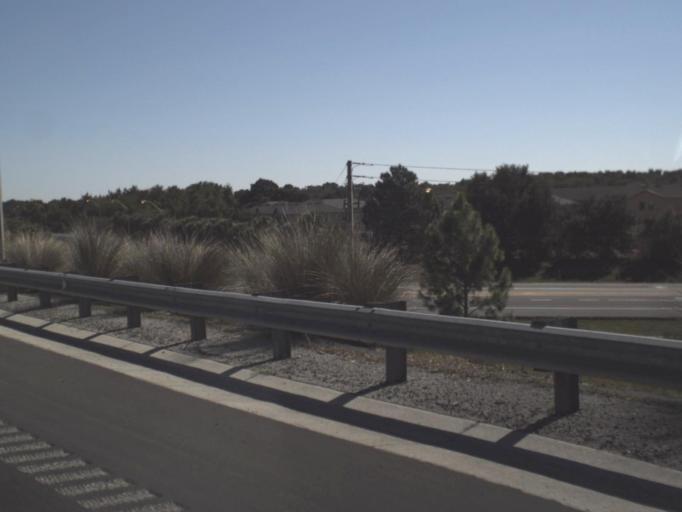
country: US
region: Florida
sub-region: Seminole County
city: Sanford
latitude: 28.7700
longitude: -81.2766
